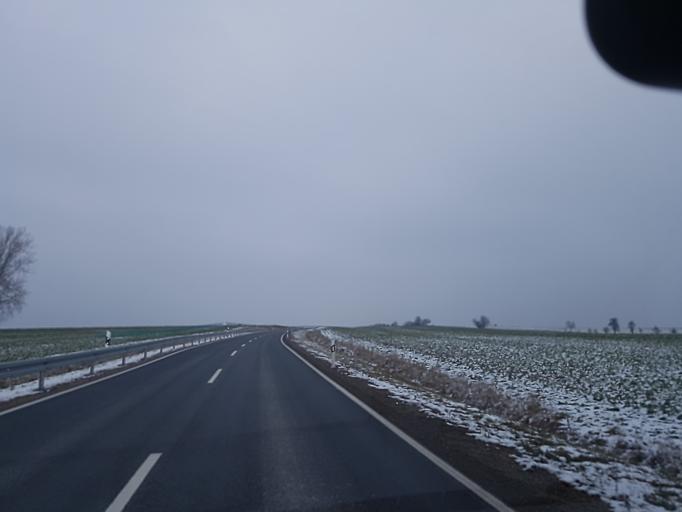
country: DE
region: Saxony
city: Bockelwitz
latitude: 51.2094
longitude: 12.9901
